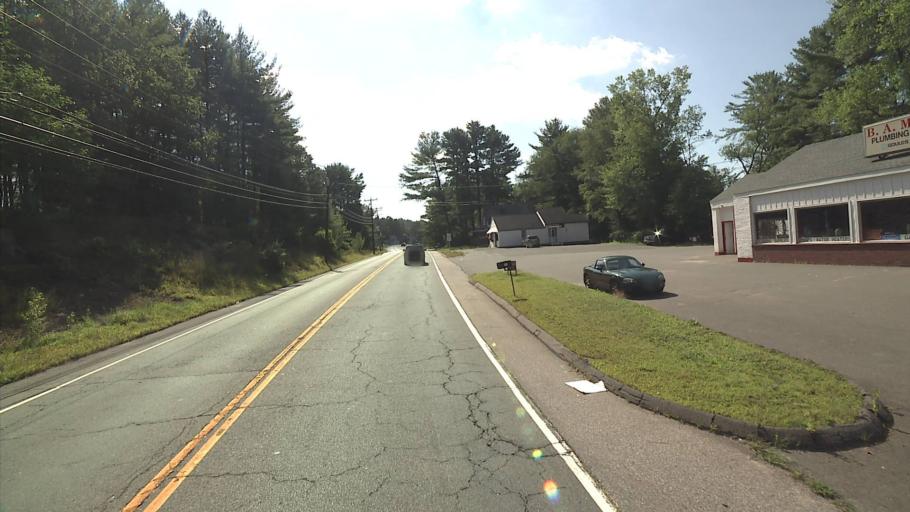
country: US
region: Connecticut
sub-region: Tolland County
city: Stafford Springs
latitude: 41.9642
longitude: -72.3180
